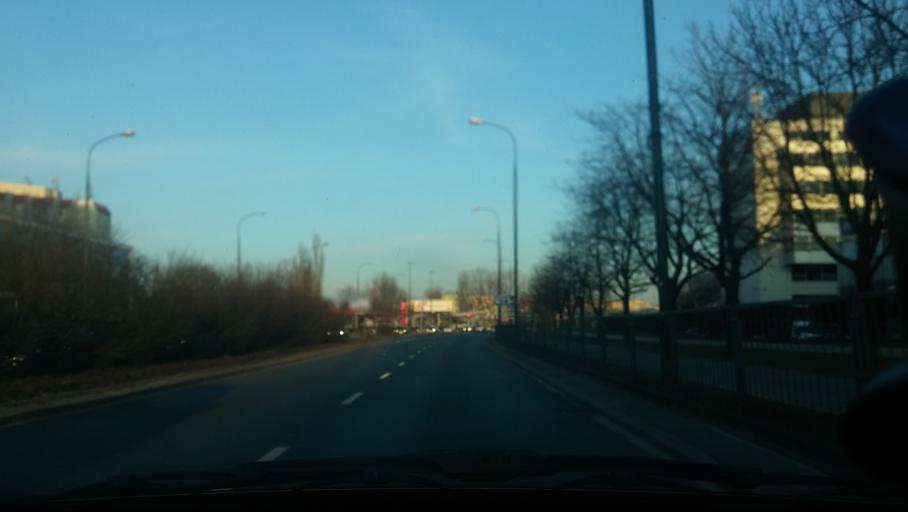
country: PL
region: Masovian Voivodeship
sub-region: Warszawa
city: Praga Poludnie
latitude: 52.2359
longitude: 21.0841
